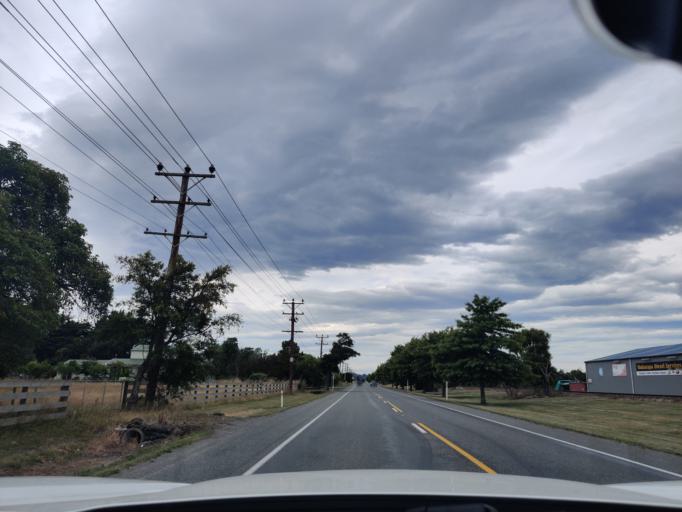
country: NZ
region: Wellington
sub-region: Masterton District
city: Masterton
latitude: -40.9562
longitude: 175.6184
